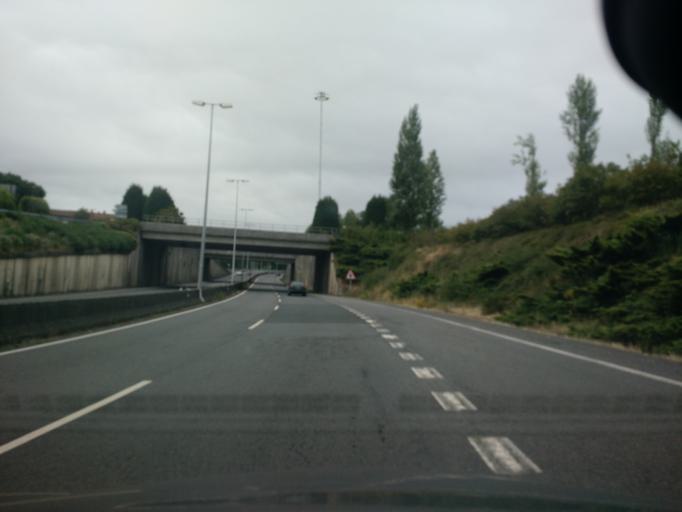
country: ES
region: Galicia
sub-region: Provincia da Coruna
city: Santiago de Compostela
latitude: 42.8876
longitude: -8.5107
